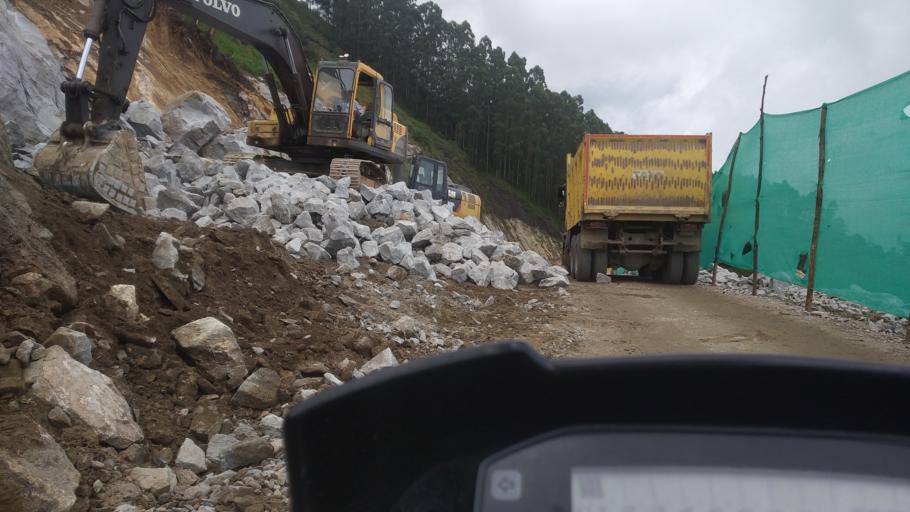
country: IN
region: Kerala
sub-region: Idukki
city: Munnar
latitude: 10.0360
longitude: 77.1374
